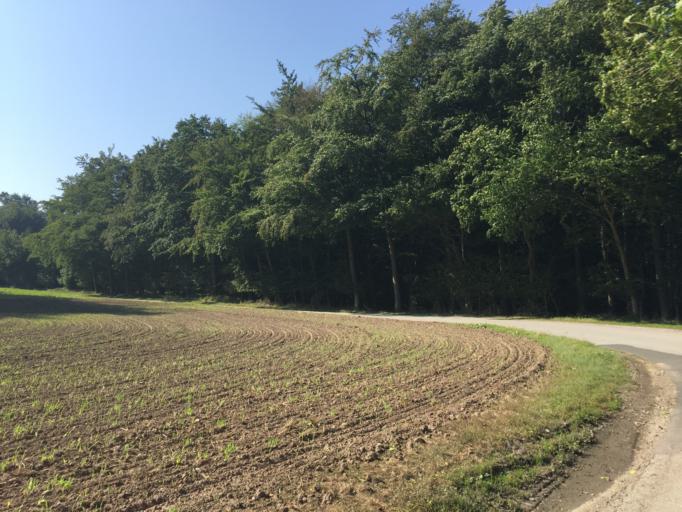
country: DK
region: South Denmark
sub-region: Langeland Kommune
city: Rudkobing
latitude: 54.8559
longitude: 10.7423
